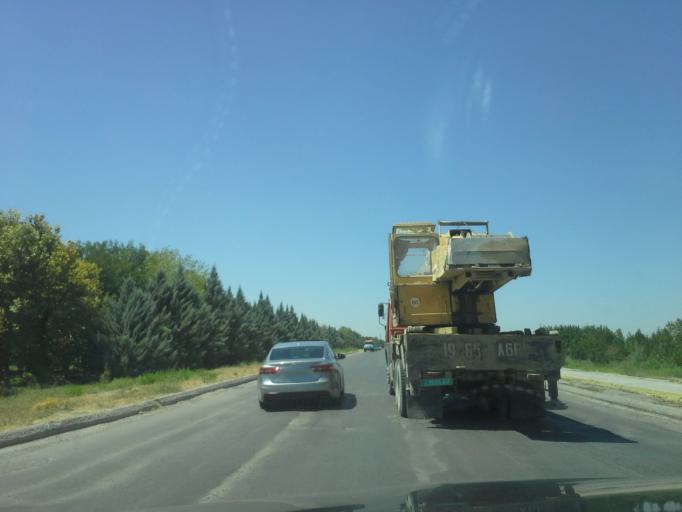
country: TM
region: Ahal
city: Abadan
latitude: 38.0284
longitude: 58.2365
